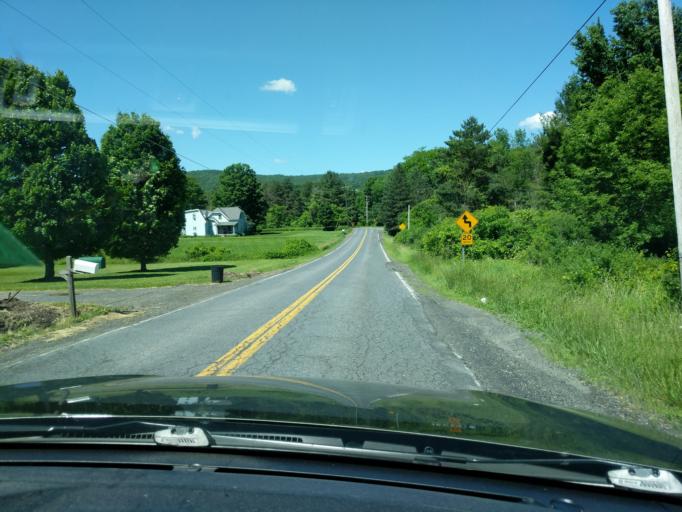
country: US
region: New York
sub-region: Tompkins County
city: East Ithaca
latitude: 42.3715
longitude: -76.3981
